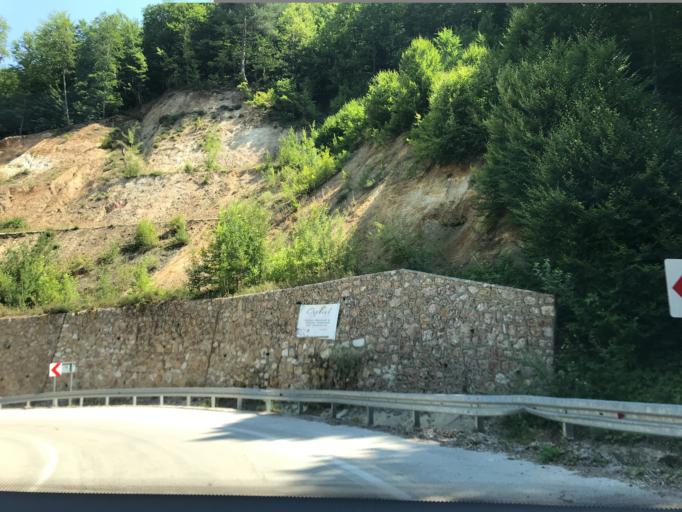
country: TR
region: Bursa
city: Tahtakopru
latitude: 39.9307
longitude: 29.5891
